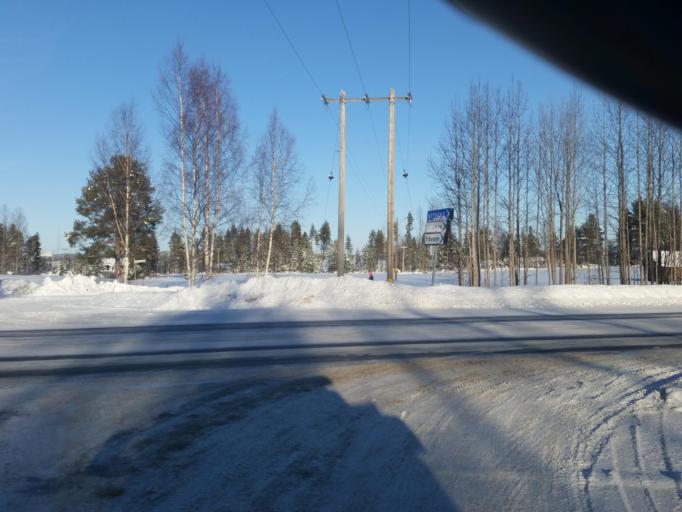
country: SE
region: Norrbotten
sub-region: Pitea Kommun
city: Bergsviken
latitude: 65.3143
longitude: 21.3326
